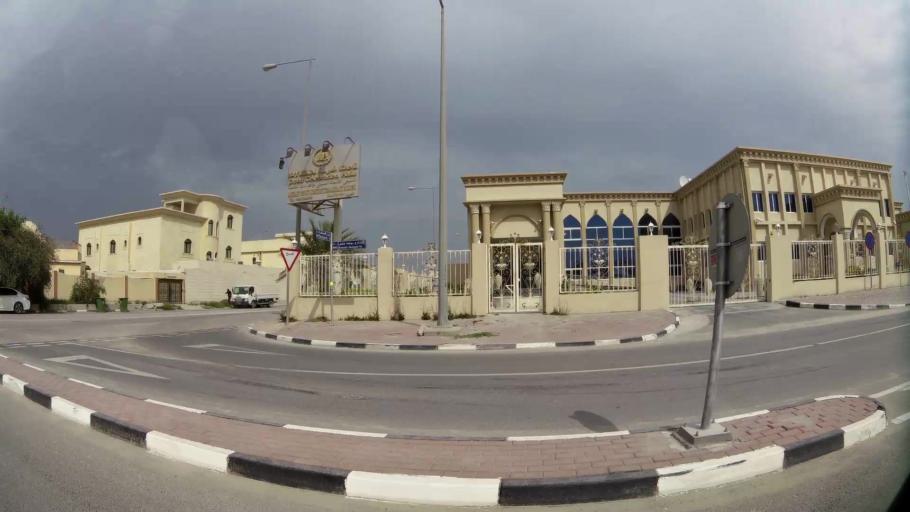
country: QA
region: Baladiyat ad Dawhah
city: Doha
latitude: 25.3386
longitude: 51.5044
